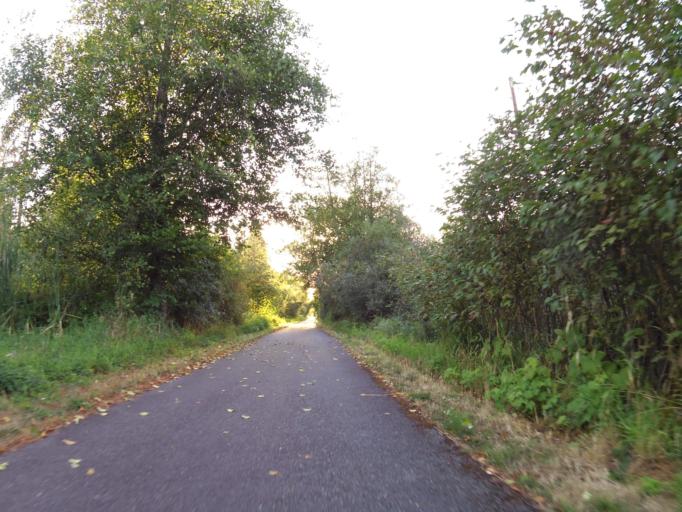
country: US
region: Washington
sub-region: Thurston County
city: Tenino
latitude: 46.8577
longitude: -122.8191
